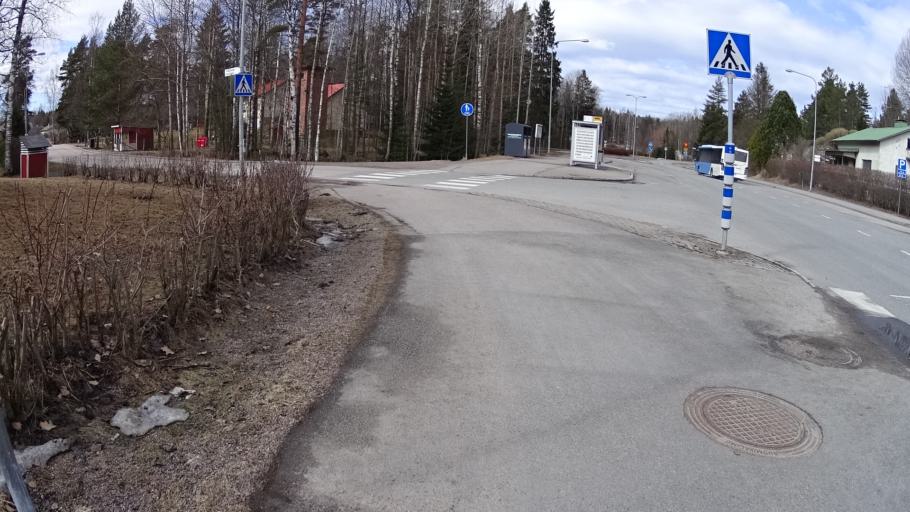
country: FI
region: Uusimaa
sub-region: Helsinki
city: Kilo
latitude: 60.2489
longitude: 24.8053
